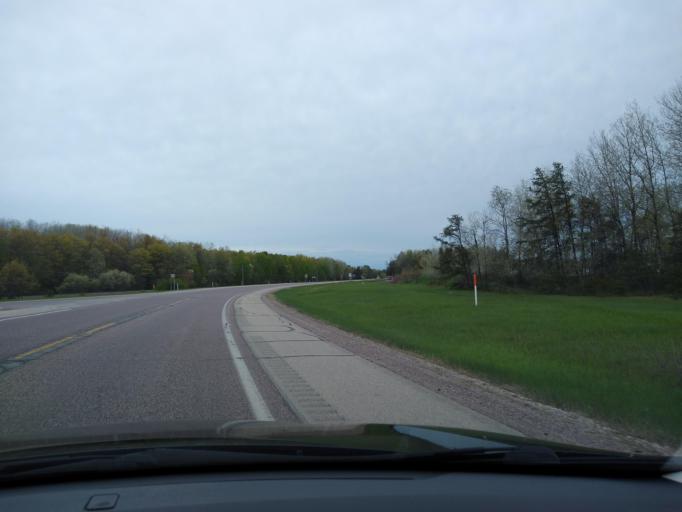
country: US
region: Michigan
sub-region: Delta County
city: Gladstone
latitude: 45.8574
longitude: -87.0614
